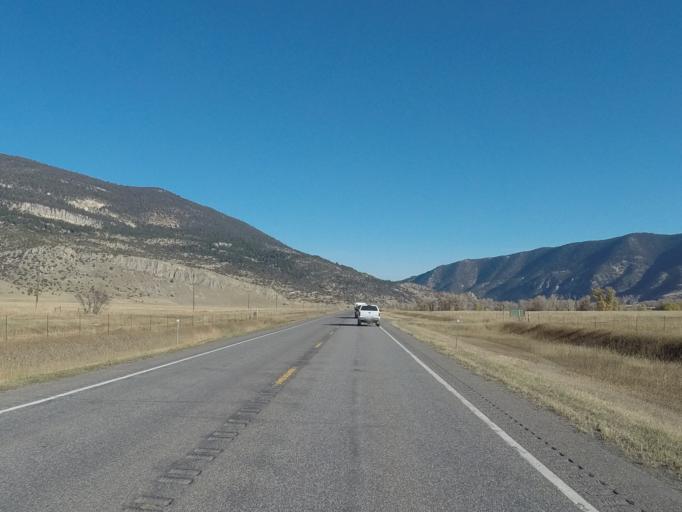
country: US
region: Montana
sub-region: Park County
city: Livingston
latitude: 45.5620
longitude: -110.5927
